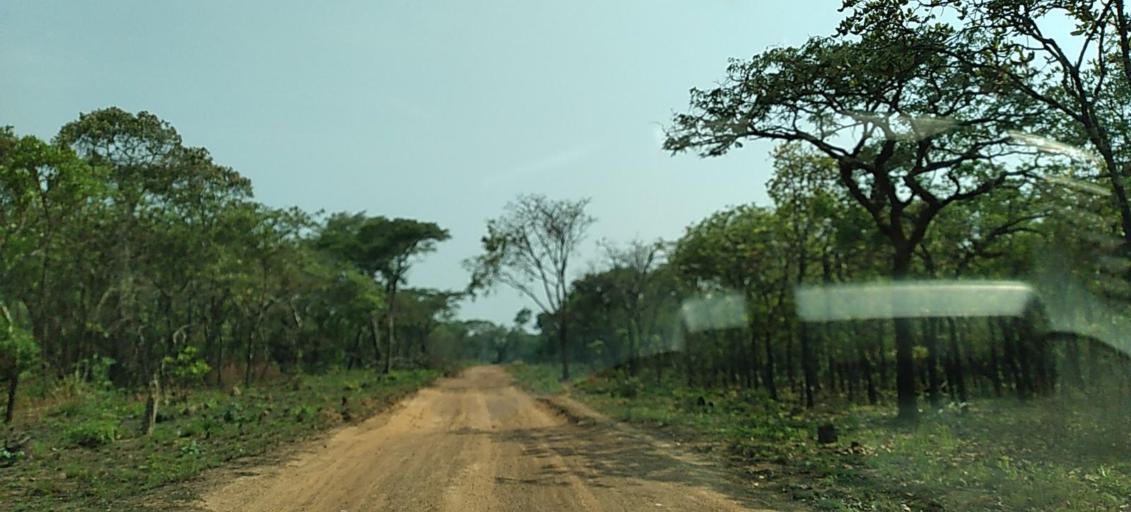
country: ZM
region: North-Western
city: Kansanshi
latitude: -12.0878
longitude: 26.8880
